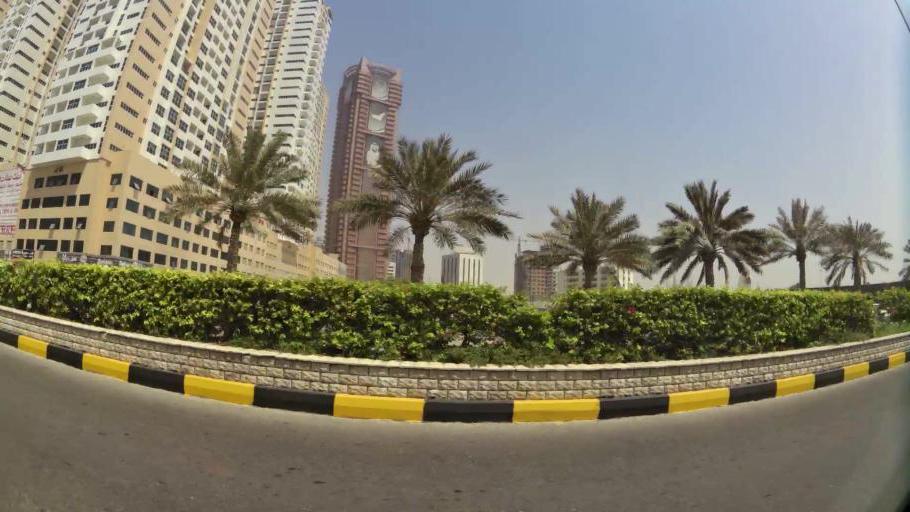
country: AE
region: Ajman
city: Ajman
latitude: 25.3948
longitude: 55.4287
